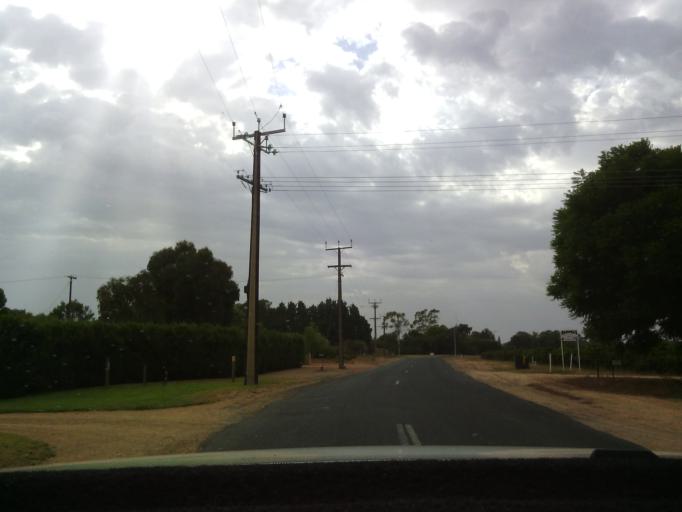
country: AU
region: South Australia
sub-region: Berri and Barmera
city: Berri
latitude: -34.2639
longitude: 140.5831
